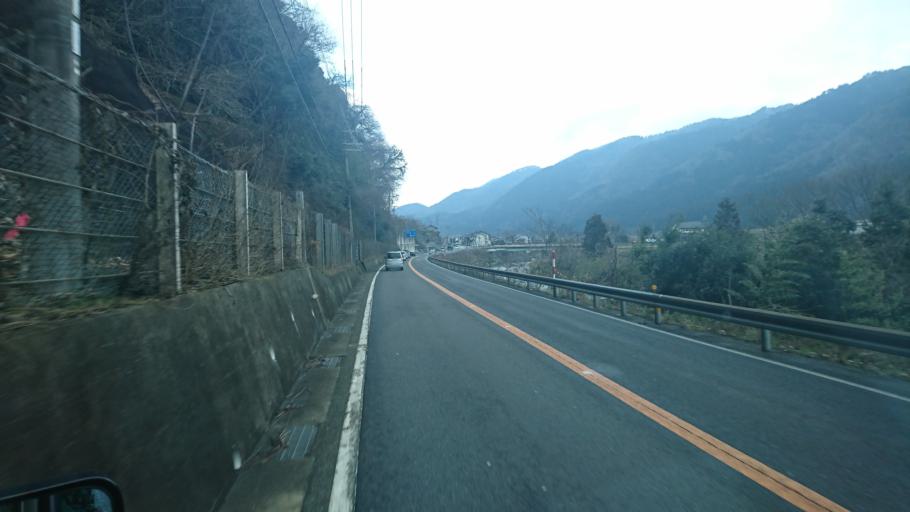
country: JP
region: Hyogo
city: Toyooka
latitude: 35.3852
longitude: 134.7088
